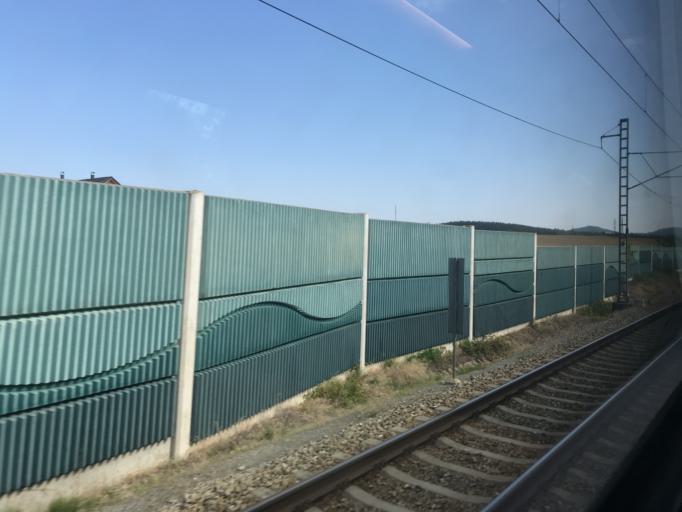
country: CZ
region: Central Bohemia
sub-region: Okres Benesov
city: Benesov
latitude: 49.7919
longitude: 14.6960
